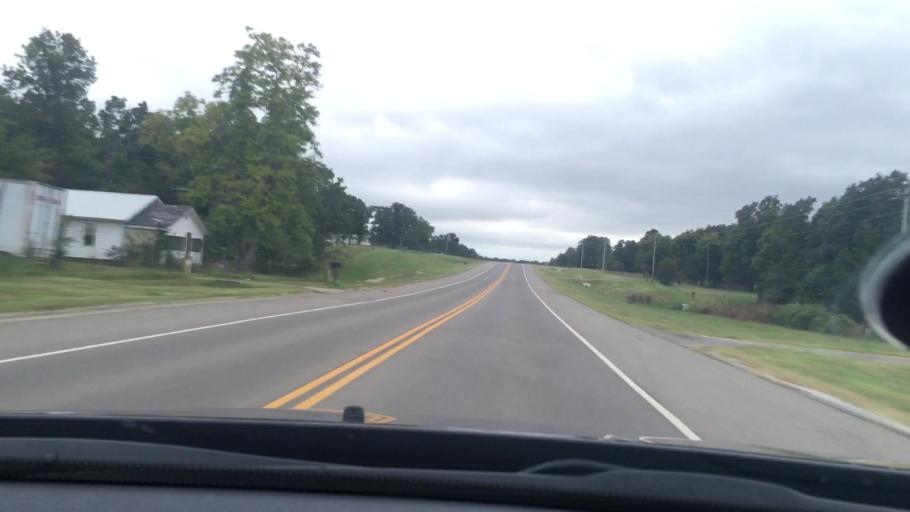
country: US
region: Oklahoma
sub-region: Sequoyah County
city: Vian
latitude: 35.6033
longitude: -94.9763
